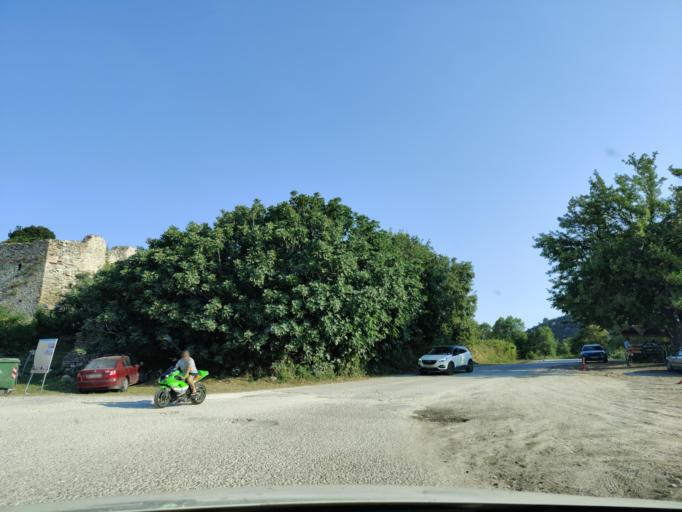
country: GR
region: East Macedonia and Thrace
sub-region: Nomos Kavalas
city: Nea Peramos
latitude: 40.8259
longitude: 24.3076
